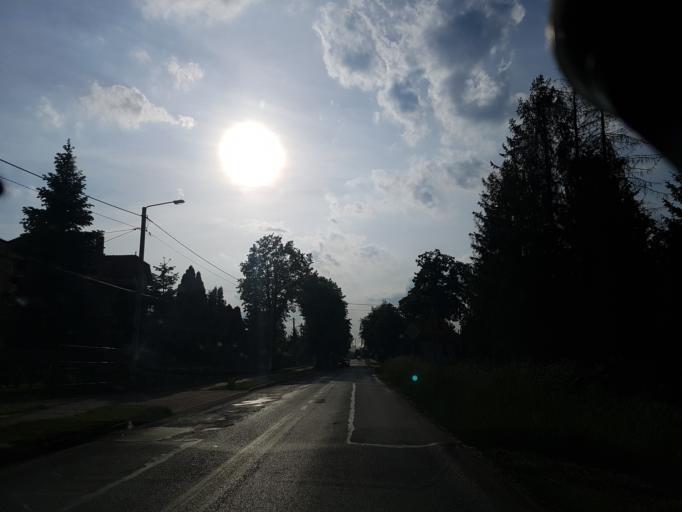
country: PL
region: Lower Silesian Voivodeship
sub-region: Powiat wroclawski
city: Kobierzyce
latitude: 50.9183
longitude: 16.9605
